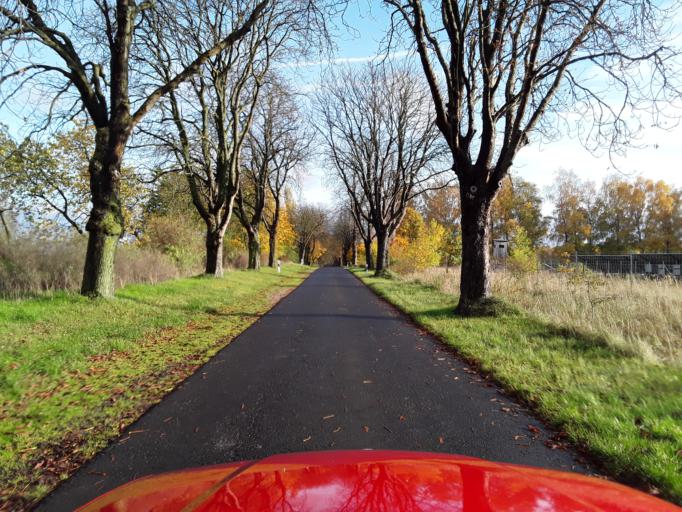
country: DE
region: Brandenburg
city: Mittenwalde
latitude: 53.2695
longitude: 13.7020
